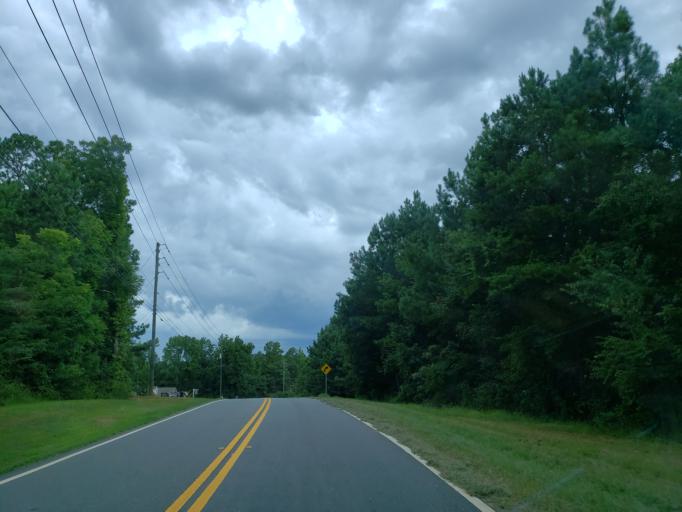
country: US
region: Georgia
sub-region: Paulding County
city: Dallas
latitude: 33.9933
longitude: -84.7955
